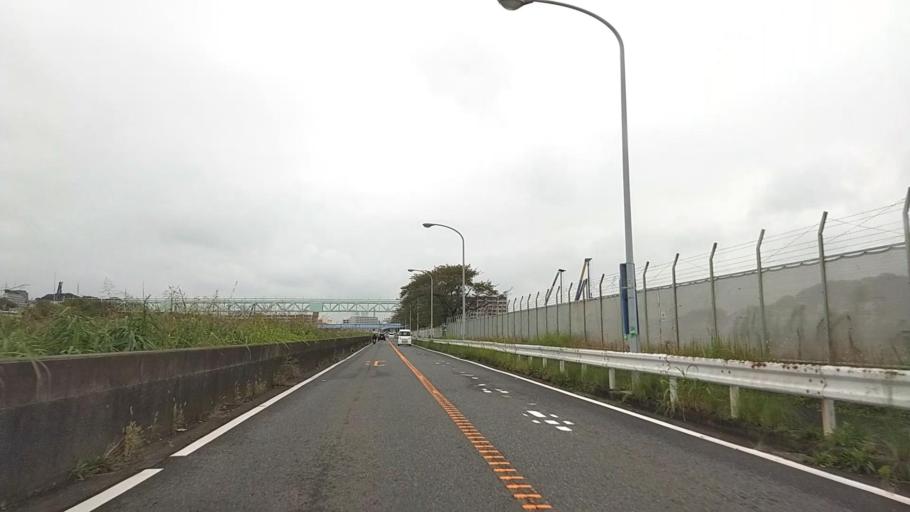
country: JP
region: Kanagawa
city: Fujisawa
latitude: 35.3895
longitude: 139.5330
